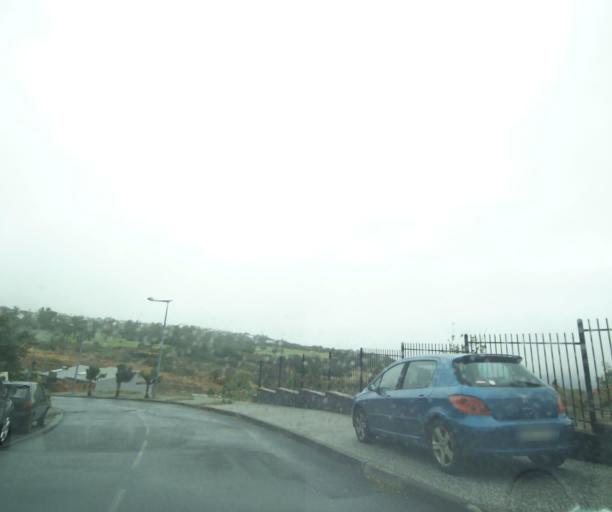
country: RE
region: Reunion
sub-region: Reunion
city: Saint-Paul
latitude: -21.0467
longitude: 55.2597
